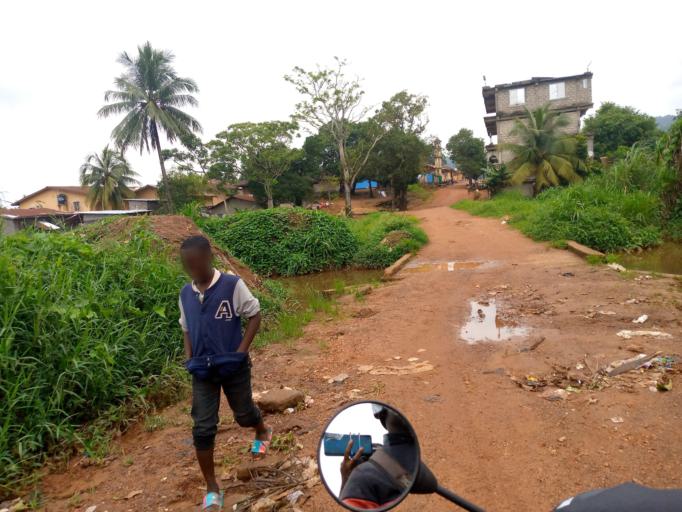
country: SL
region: Eastern Province
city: Kenema
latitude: 7.8645
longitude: -11.1900
